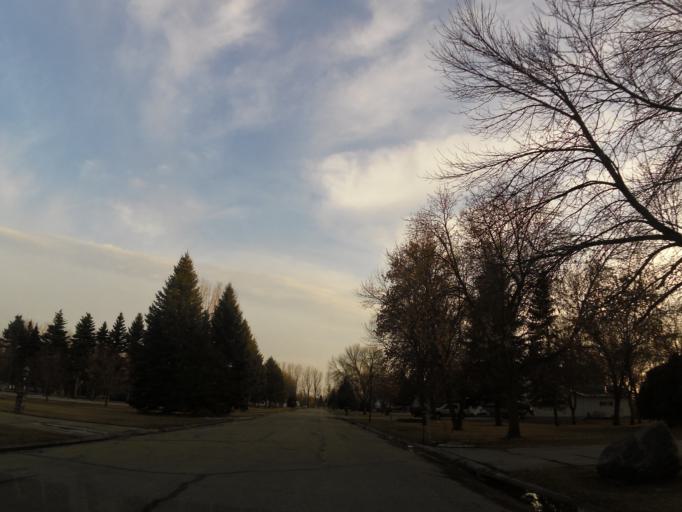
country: US
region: North Dakota
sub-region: Grand Forks County
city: Grand Forks
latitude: 47.8560
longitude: -97.0116
